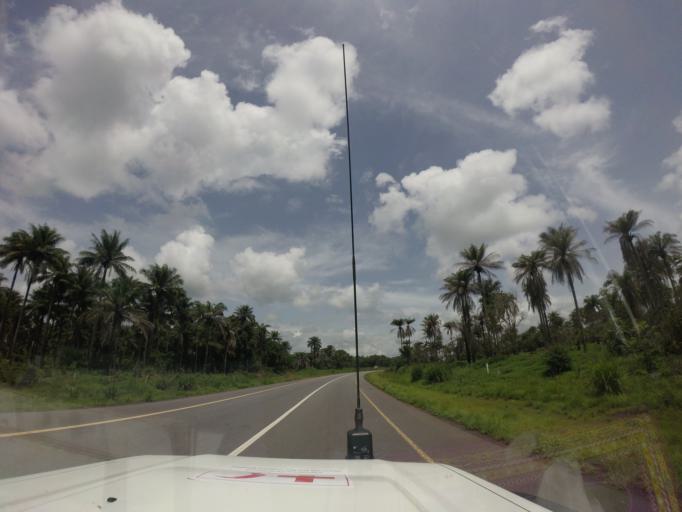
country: SL
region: Northern Province
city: Mange
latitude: 8.9015
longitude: -12.8371
